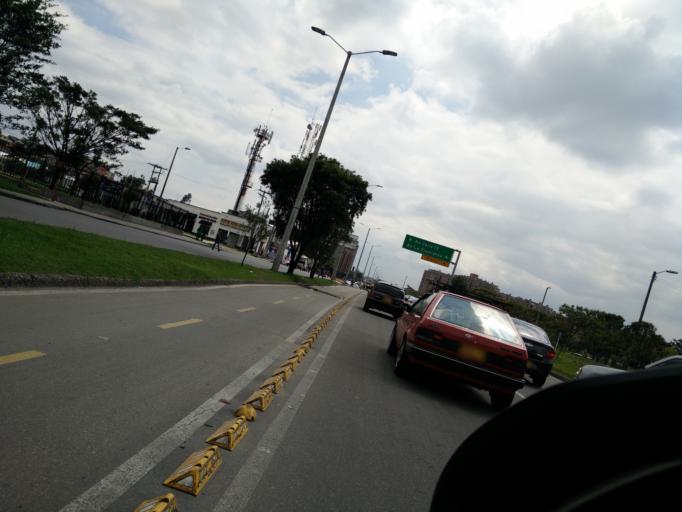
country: CO
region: Bogota D.C.
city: Bogota
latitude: 4.6390
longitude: -74.0959
